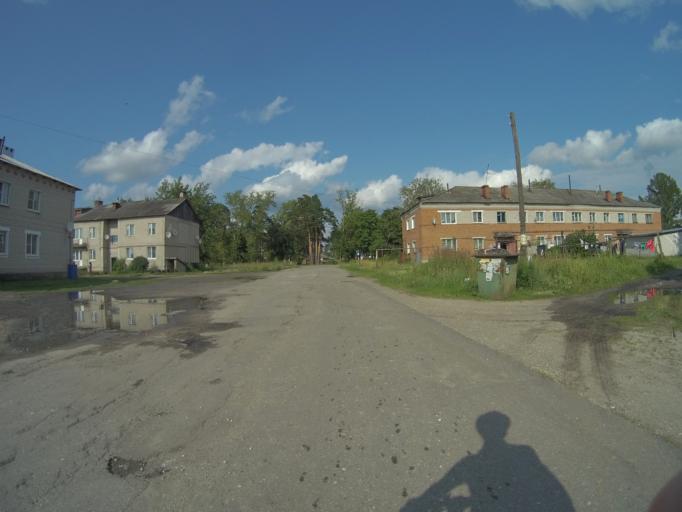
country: RU
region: Vladimir
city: Orgtrud
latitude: 56.2862
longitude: 40.7787
